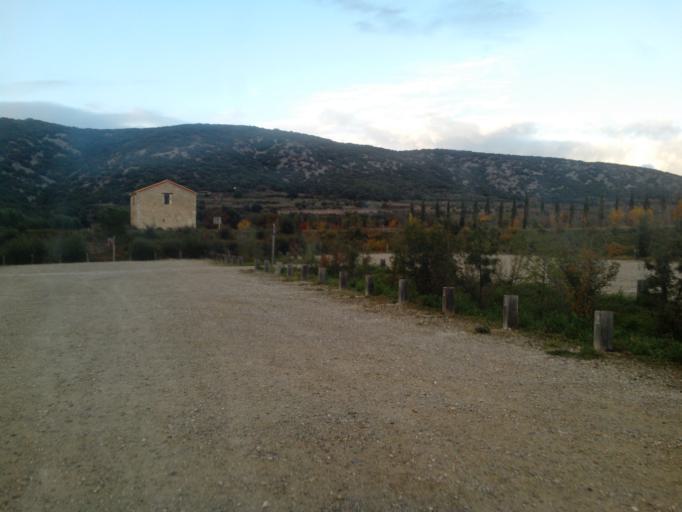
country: FR
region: Languedoc-Roussillon
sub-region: Departement de l'Herault
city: Saint-Jean-de-Fos
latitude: 43.7025
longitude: 3.5625
